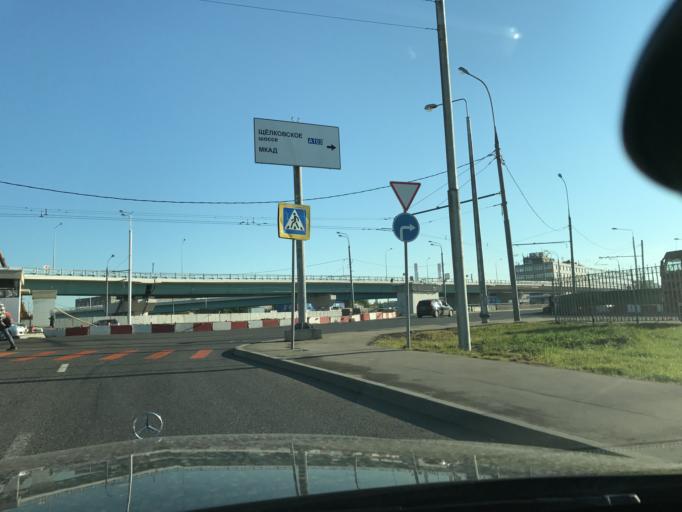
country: RU
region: Moskovskaya
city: Bogorodskoye
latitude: 55.8011
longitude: 37.7494
